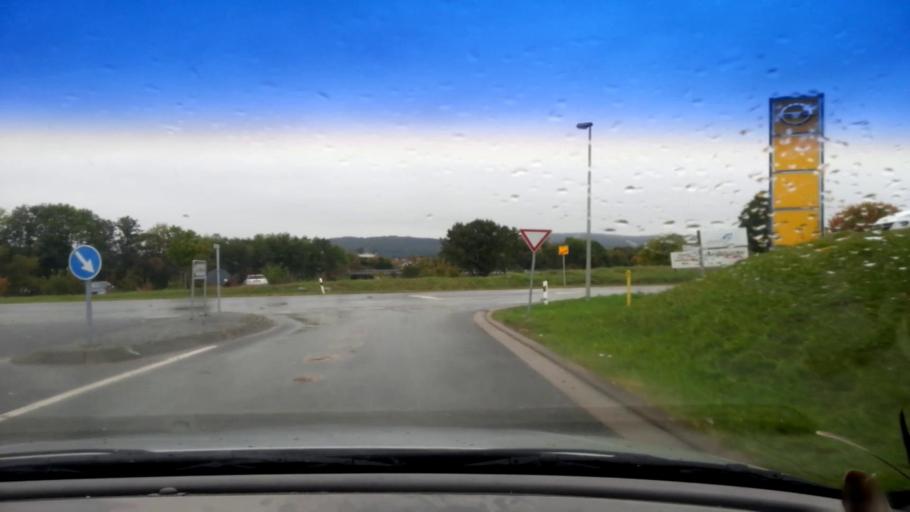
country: DE
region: Bavaria
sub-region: Upper Franconia
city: Schesslitz
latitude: 49.9803
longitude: 11.0431
